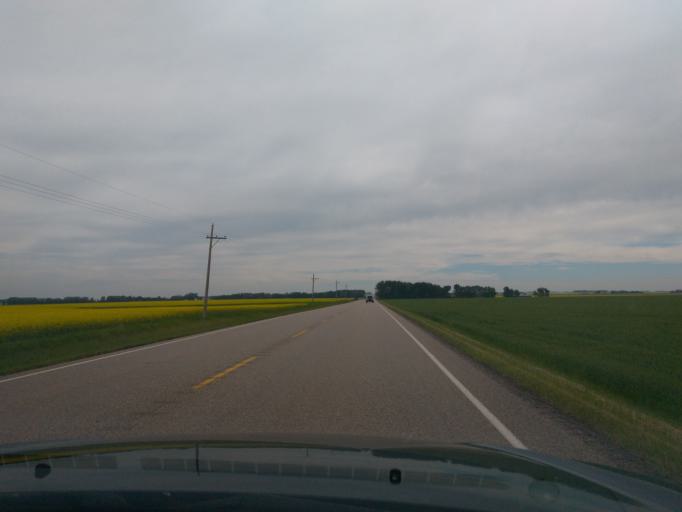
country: CA
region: Alberta
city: Crossfield
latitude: 51.5614
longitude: -113.9291
